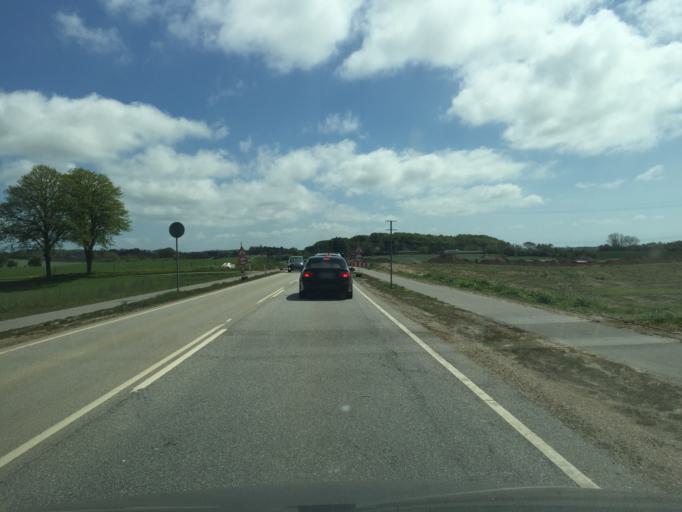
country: DK
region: Zealand
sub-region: Vordingborg Kommune
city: Nyrad
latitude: 54.9991
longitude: 11.9982
